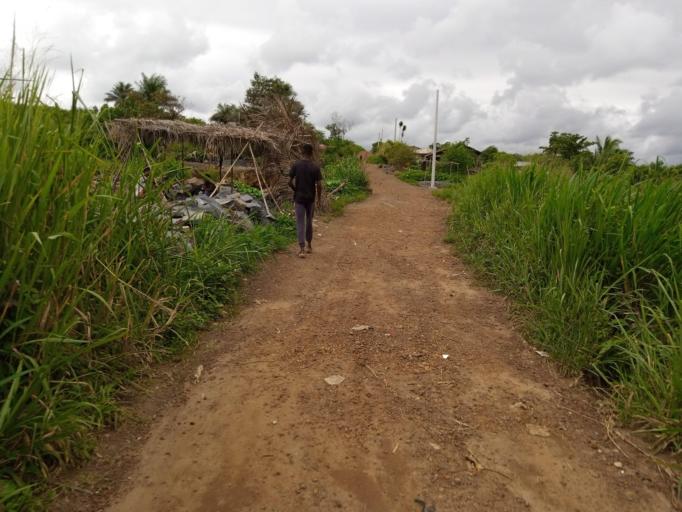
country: SL
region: Southern Province
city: Moyamba
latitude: 8.1706
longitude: -12.4268
